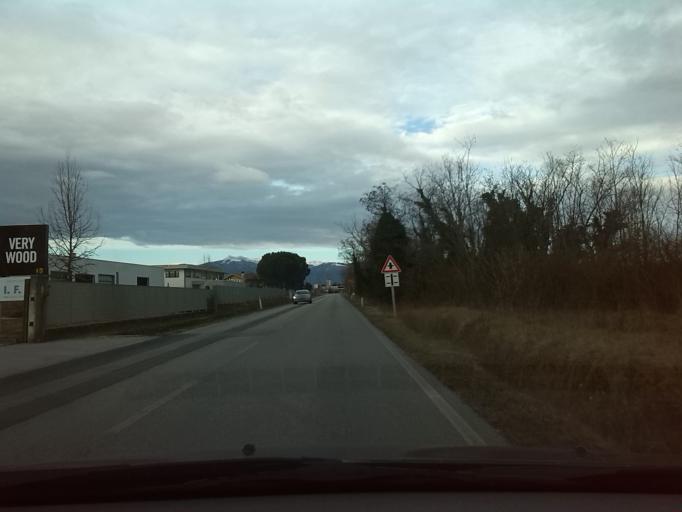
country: IT
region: Friuli Venezia Giulia
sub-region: Provincia di Udine
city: Orsaria
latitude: 46.0264
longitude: 13.3966
